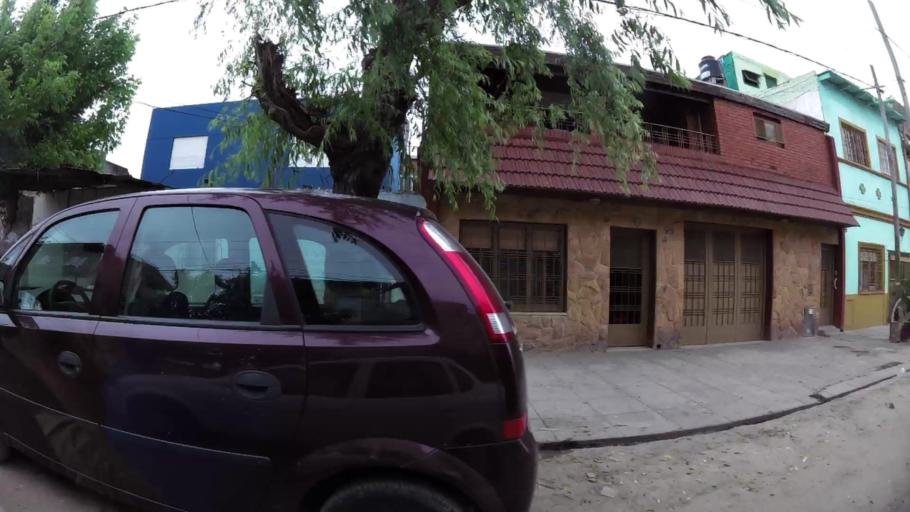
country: AR
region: Buenos Aires
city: San Justo
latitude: -34.6735
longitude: -58.5213
